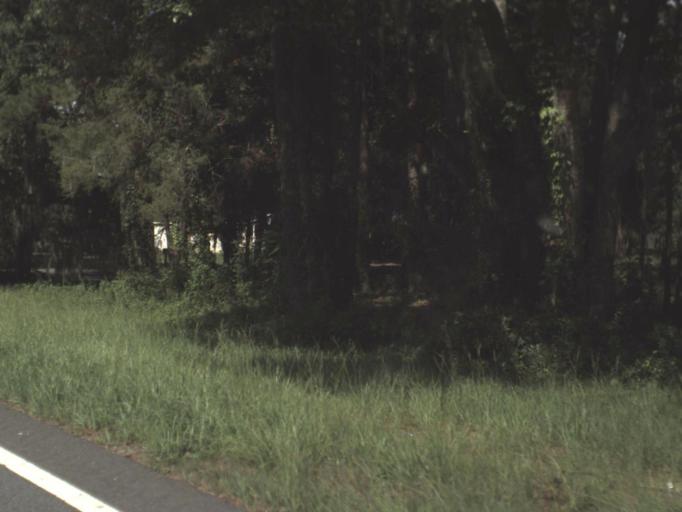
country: US
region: Florida
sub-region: Madison County
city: Madison
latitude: 30.5741
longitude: -83.3576
